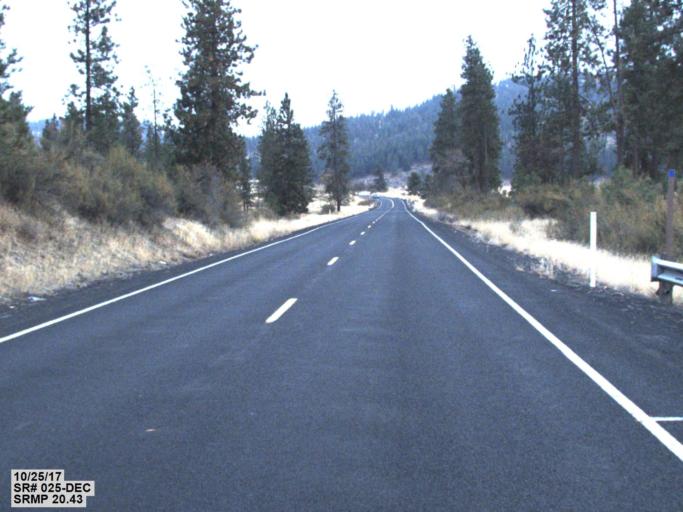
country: US
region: Washington
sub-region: Lincoln County
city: Davenport
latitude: 47.9000
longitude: -118.2744
